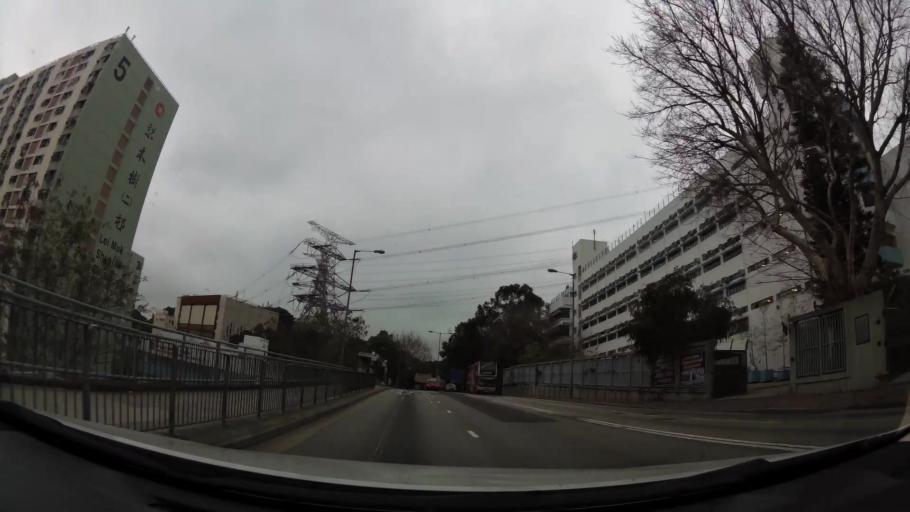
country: HK
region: Tsuen Wan
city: Tsuen Wan
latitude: 22.3802
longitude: 114.1350
